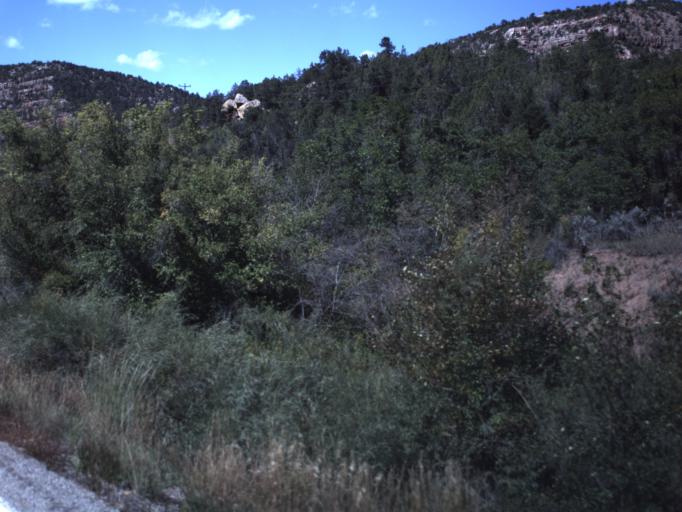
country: US
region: Utah
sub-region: Grand County
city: Moab
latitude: 38.3304
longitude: -109.0820
